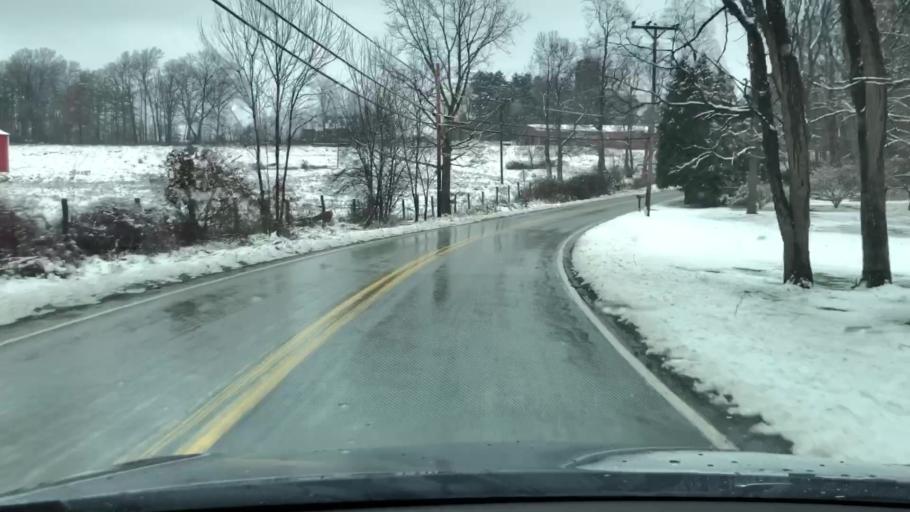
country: US
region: Pennsylvania
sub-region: Fayette County
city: Dunbar
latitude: 39.8285
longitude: -79.5373
